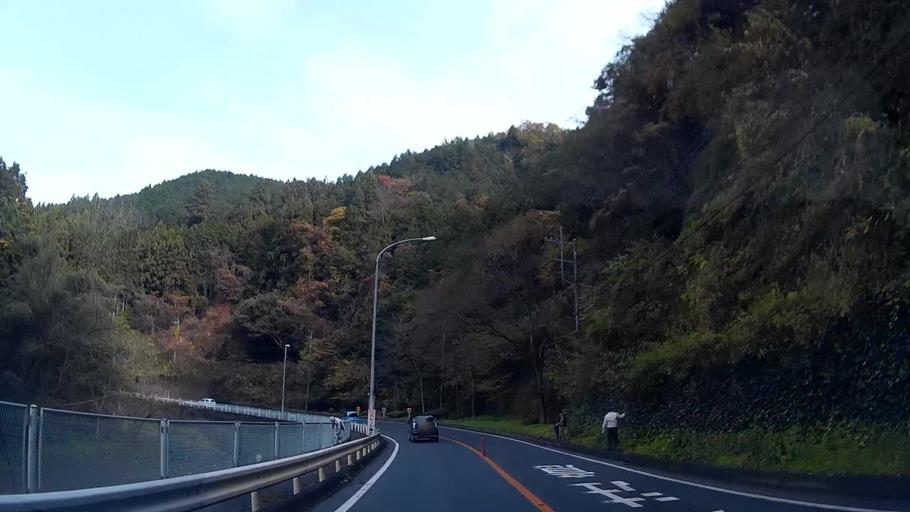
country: JP
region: Saitama
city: Morohongo
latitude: 35.9082
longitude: 139.2432
